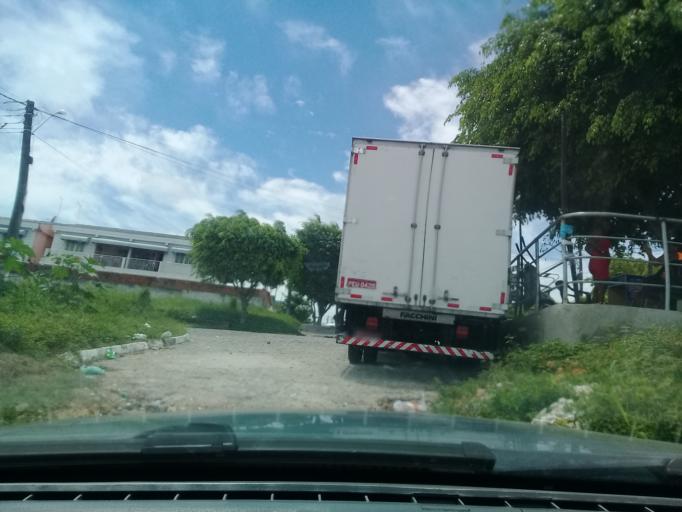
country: BR
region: Pernambuco
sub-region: Igarassu
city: Igarassu
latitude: -7.8454
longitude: -34.9083
